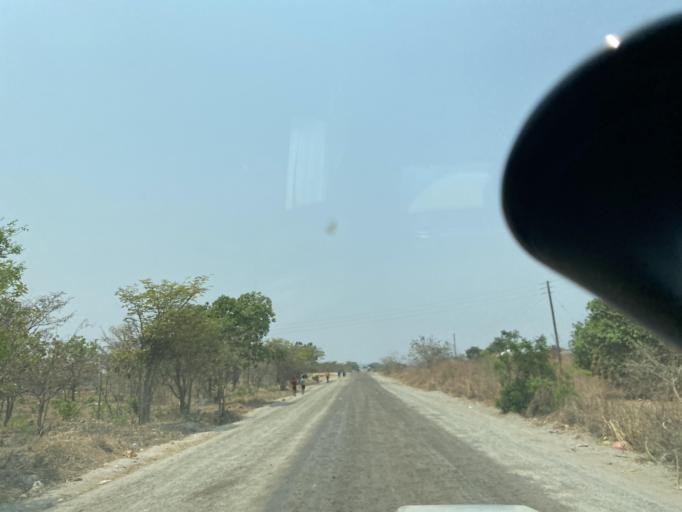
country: ZM
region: Lusaka
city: Lusaka
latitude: -15.5613
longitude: 28.4196
